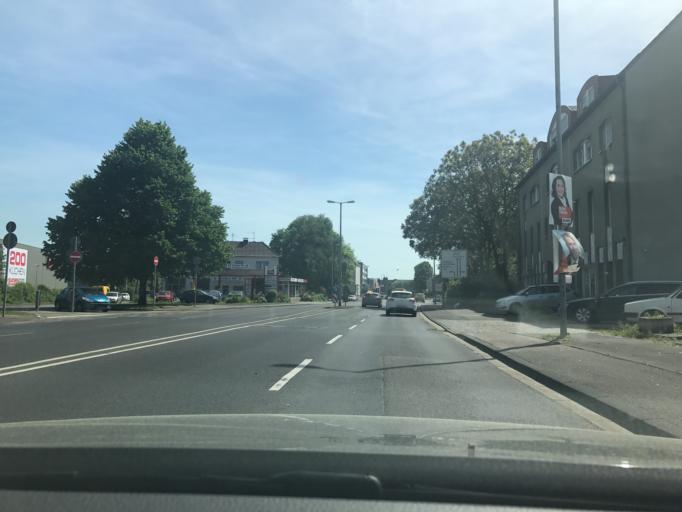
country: DE
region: North Rhine-Westphalia
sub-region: Regierungsbezirk Dusseldorf
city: Monchengladbach
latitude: 51.1862
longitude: 6.4440
